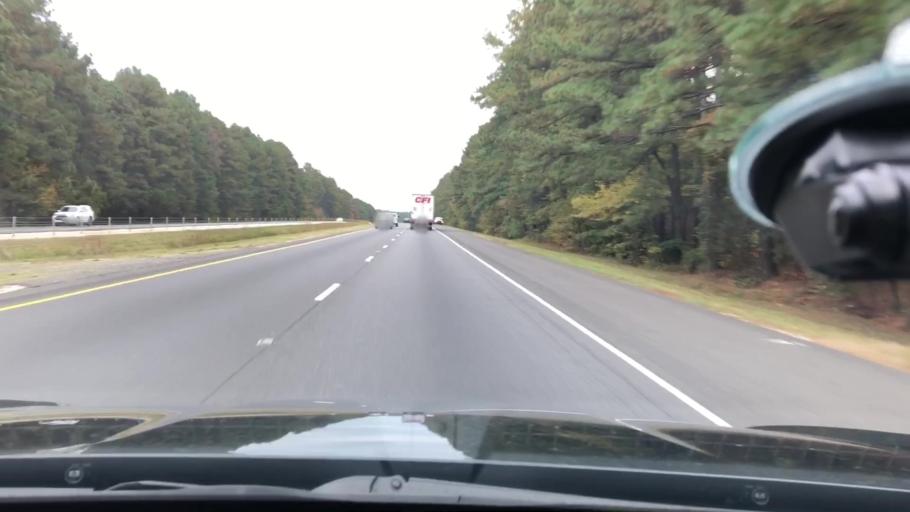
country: US
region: Arkansas
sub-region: Hot Spring County
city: Malvern
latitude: 34.2753
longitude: -92.9663
